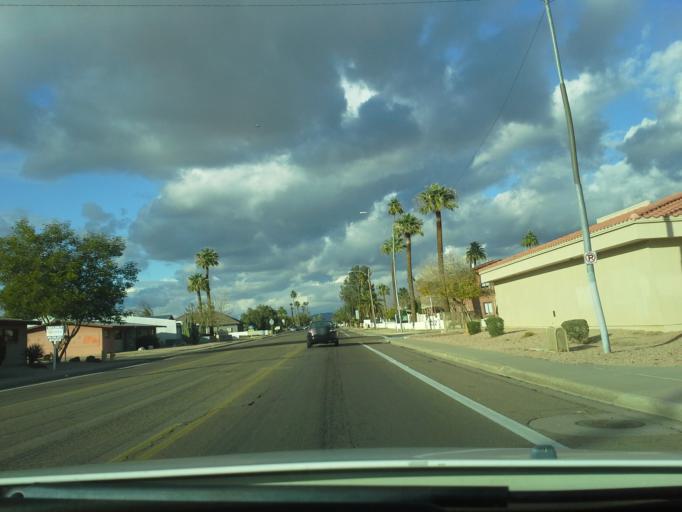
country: US
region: Arizona
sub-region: Maricopa County
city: Phoenix
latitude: 33.4890
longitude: -112.0913
